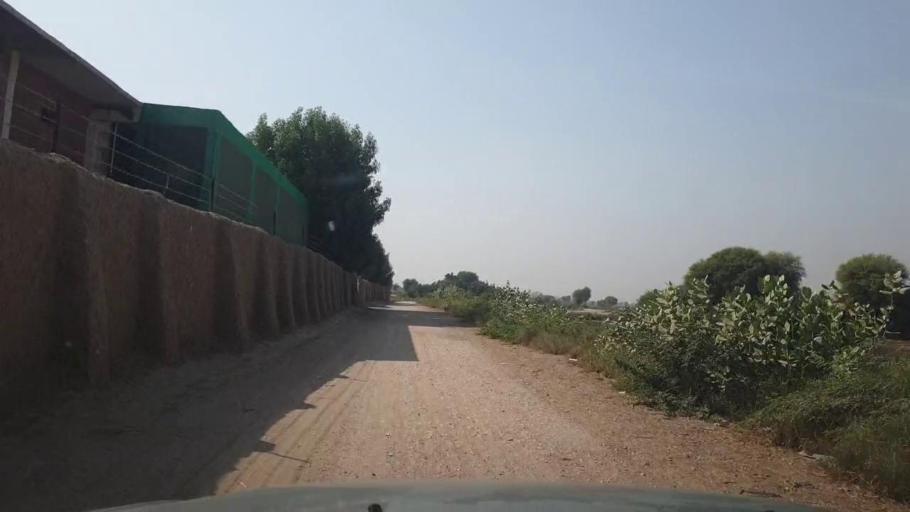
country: PK
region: Sindh
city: Bhit Shah
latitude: 25.7390
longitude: 68.5015
